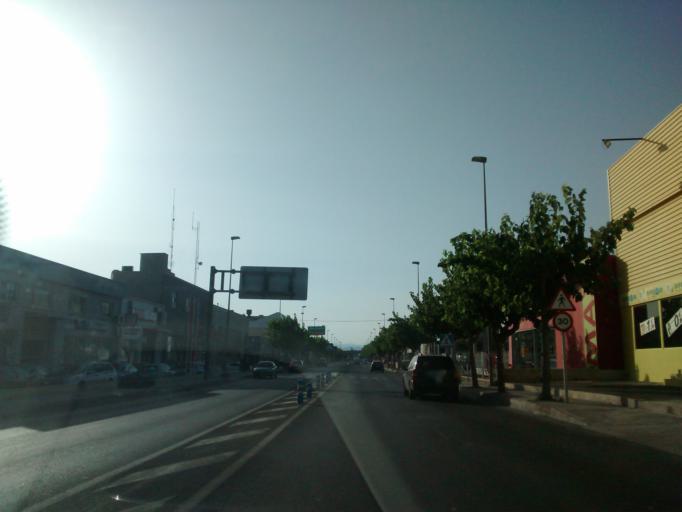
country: ES
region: Valencia
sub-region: Provincia de Alicante
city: Santa Pola
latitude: 38.1974
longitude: -0.5634
